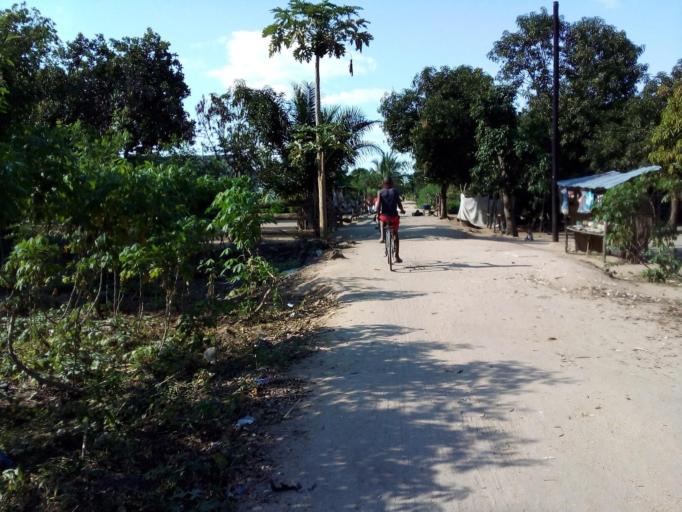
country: MZ
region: Zambezia
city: Quelimane
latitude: -17.6019
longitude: 36.8233
